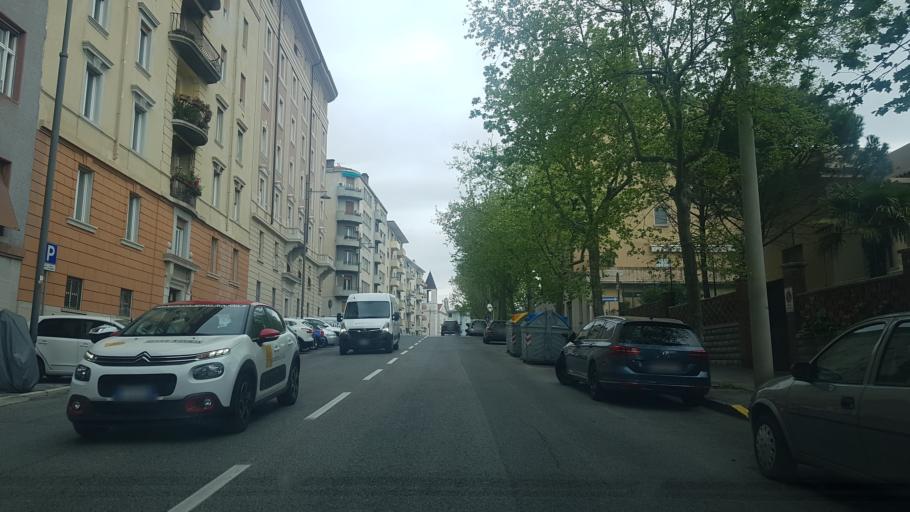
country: IT
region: Friuli Venezia Giulia
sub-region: Provincia di Trieste
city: Trieste
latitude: 45.6419
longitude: 13.7578
